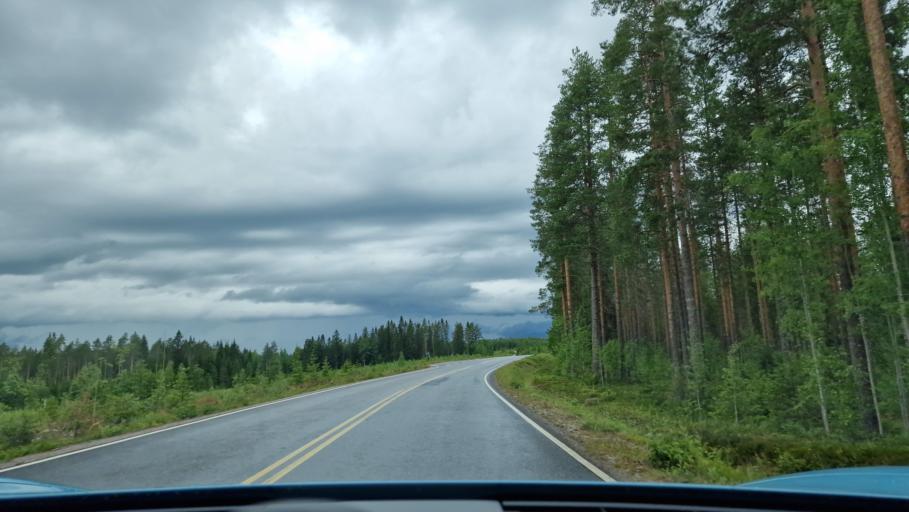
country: FI
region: Southern Ostrobothnia
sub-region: Jaerviseutu
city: Soini
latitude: 62.7080
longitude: 24.4471
